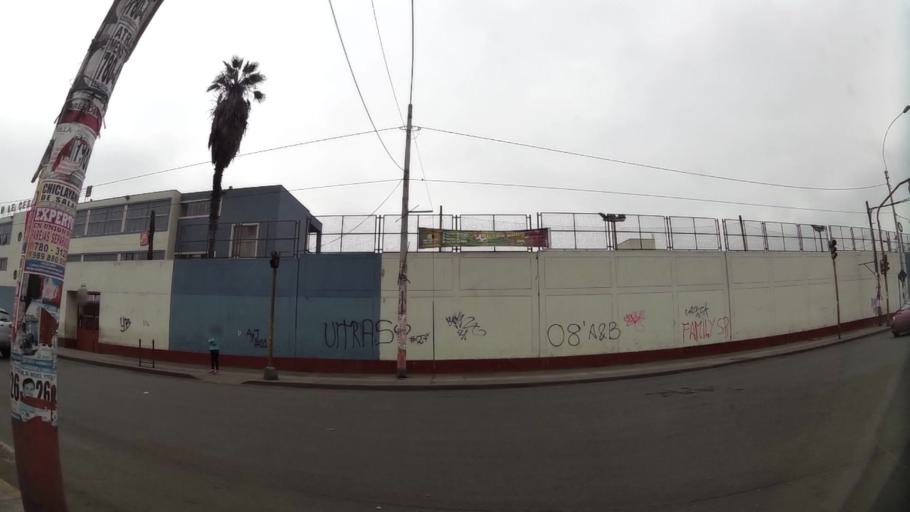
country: PE
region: Lima
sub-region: Lima
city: San Luis
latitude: -12.0681
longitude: -77.0063
